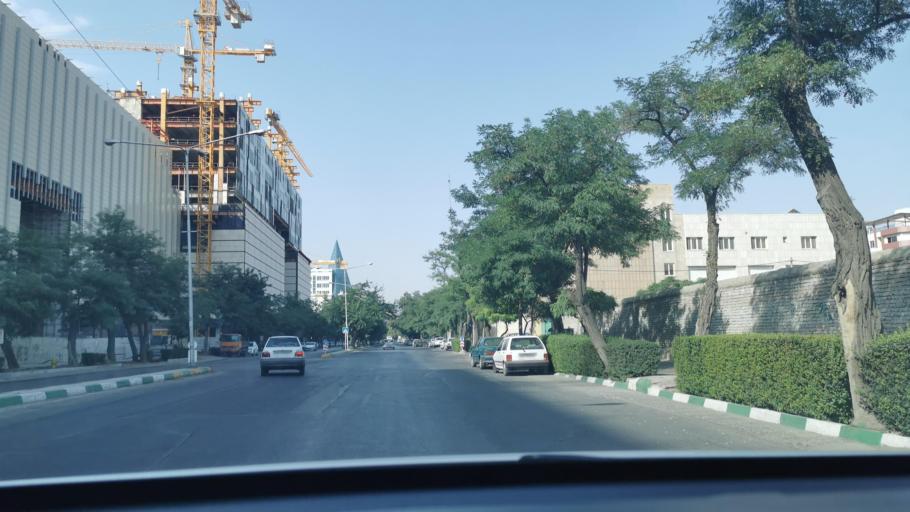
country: IR
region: Razavi Khorasan
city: Mashhad
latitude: 36.3189
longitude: 59.5612
